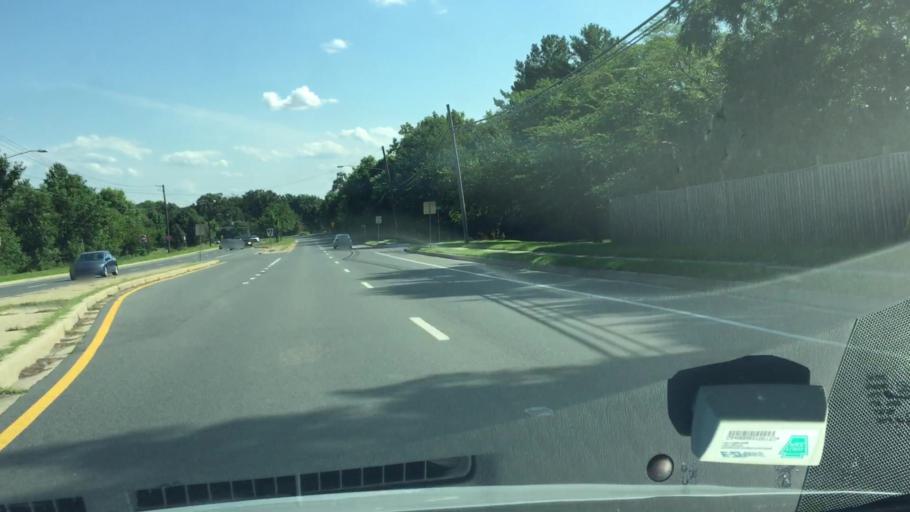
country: US
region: Maryland
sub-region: Montgomery County
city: Layhill
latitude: 39.0843
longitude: -77.0463
